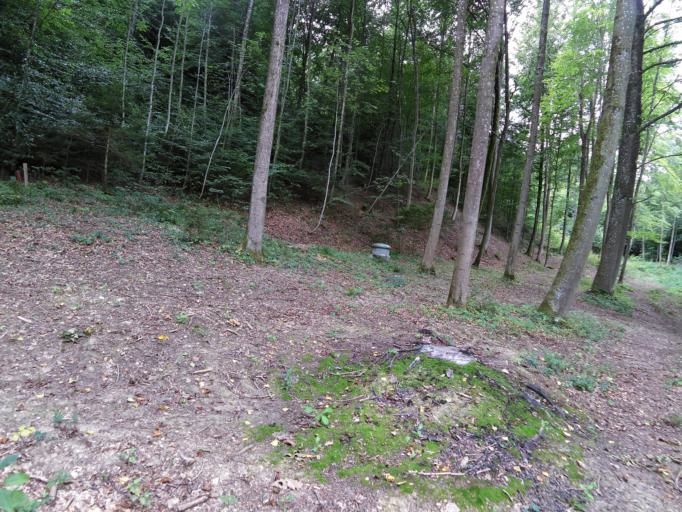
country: CH
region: Thurgau
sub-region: Kreuzlingen District
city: Ermatingen
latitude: 47.6525
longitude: 9.0633
